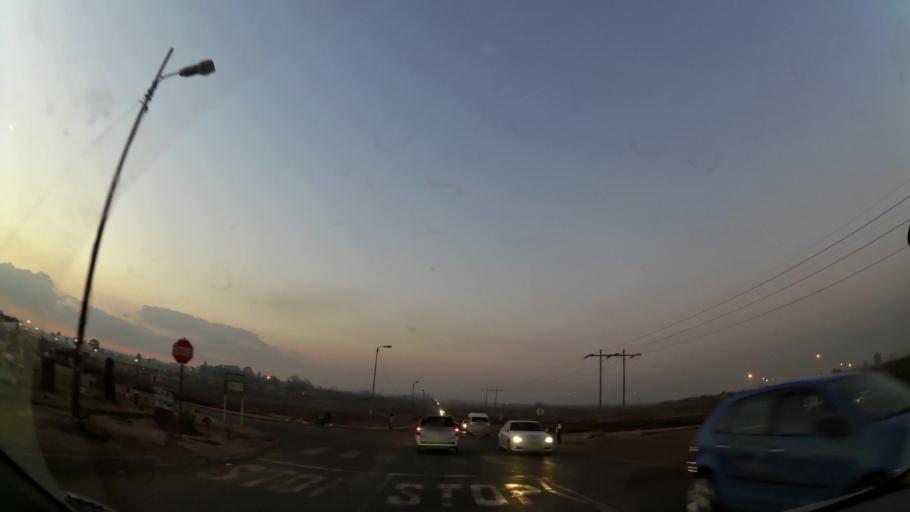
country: ZA
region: Gauteng
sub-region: Ekurhuleni Metropolitan Municipality
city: Springs
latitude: -26.3248
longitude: 28.3749
